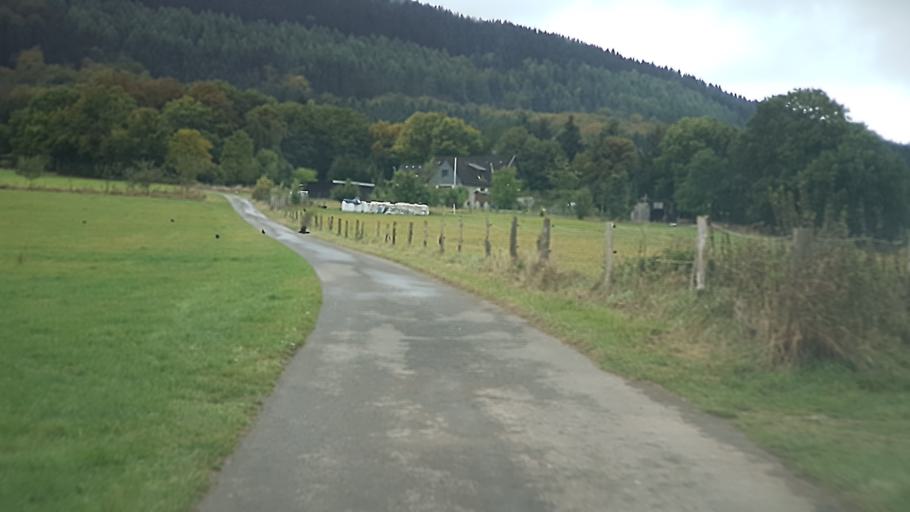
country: DE
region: North Rhine-Westphalia
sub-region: Regierungsbezirk Arnsberg
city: Herscheid
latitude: 51.1599
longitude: 7.7674
